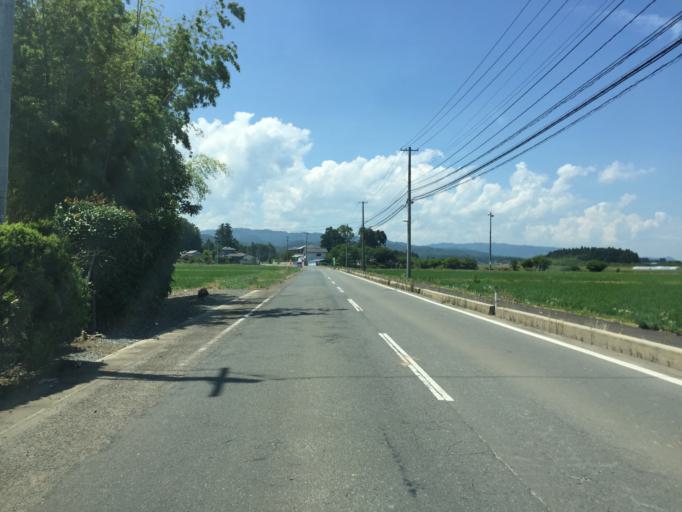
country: JP
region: Fukushima
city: Namie
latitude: 37.7164
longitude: 140.9393
